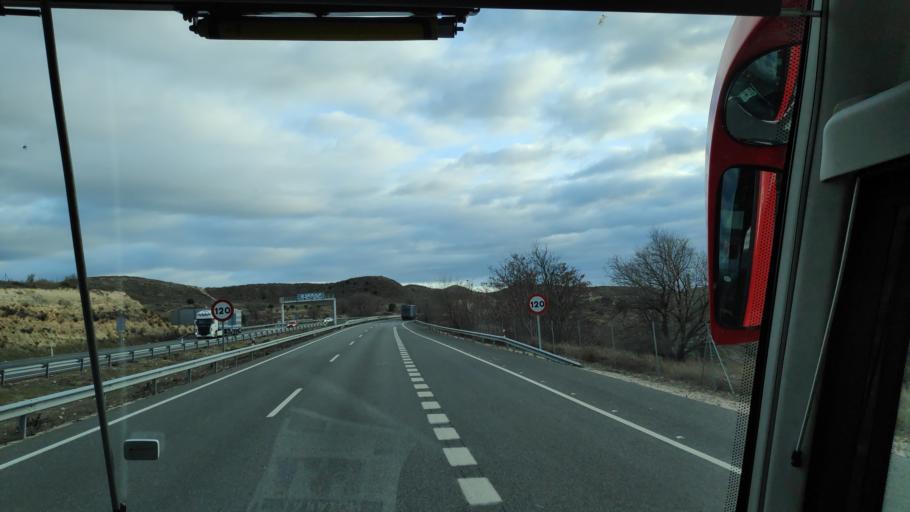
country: ES
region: Madrid
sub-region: Provincia de Madrid
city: Perales de Tajuna
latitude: 40.2210
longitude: -3.3303
